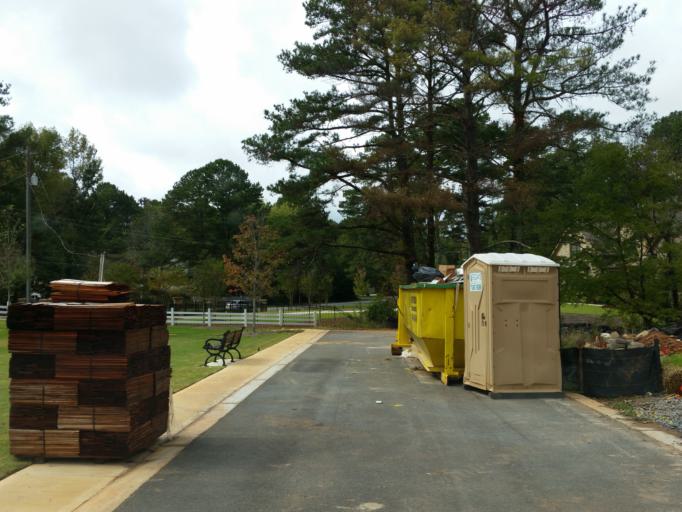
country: US
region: Georgia
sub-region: Fulton County
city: Roswell
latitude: 34.0074
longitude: -84.4585
